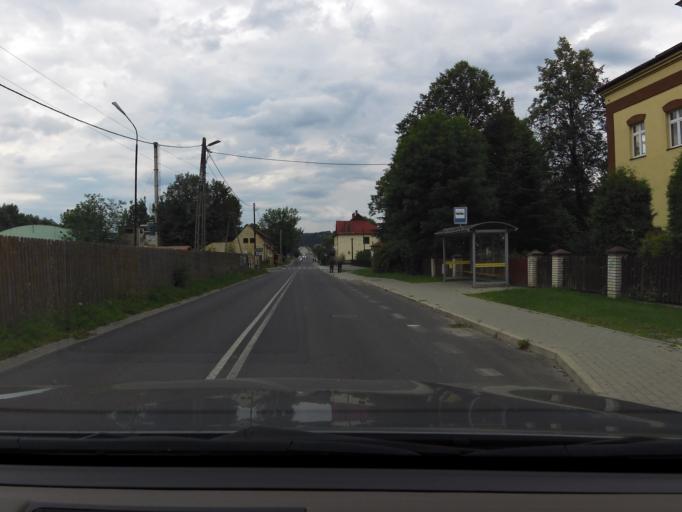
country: PL
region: Silesian Voivodeship
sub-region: Powiat zywiecki
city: Ujsoly
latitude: 49.4781
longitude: 19.1434
